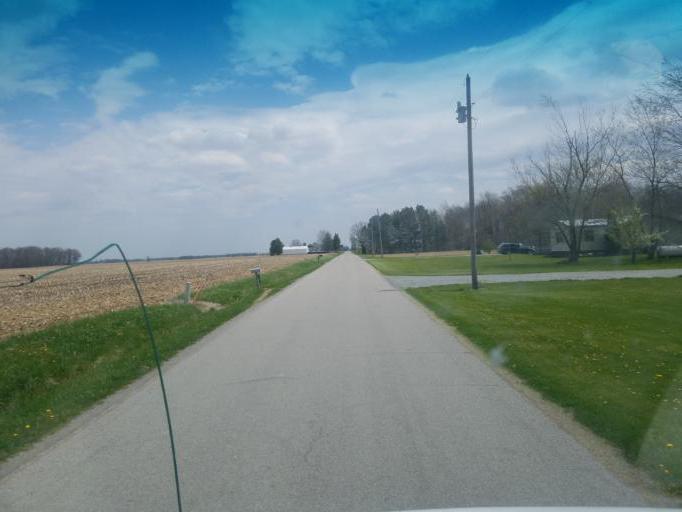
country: US
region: Ohio
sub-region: Wyandot County
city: Upper Sandusky
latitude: 40.7888
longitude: -83.3217
